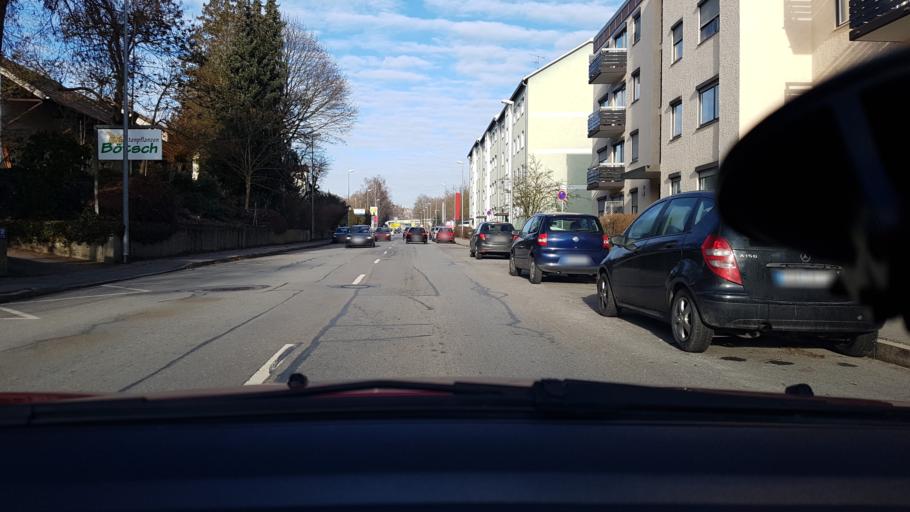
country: DE
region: Bavaria
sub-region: Lower Bavaria
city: Pfarrkirchen
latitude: 48.4380
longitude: 12.9366
